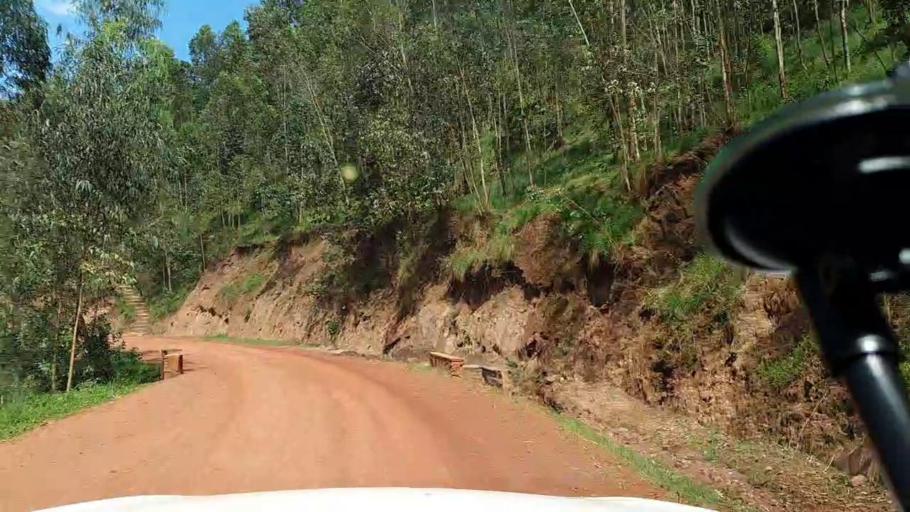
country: RW
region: Kigali
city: Kigali
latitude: -1.7998
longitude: 29.8898
